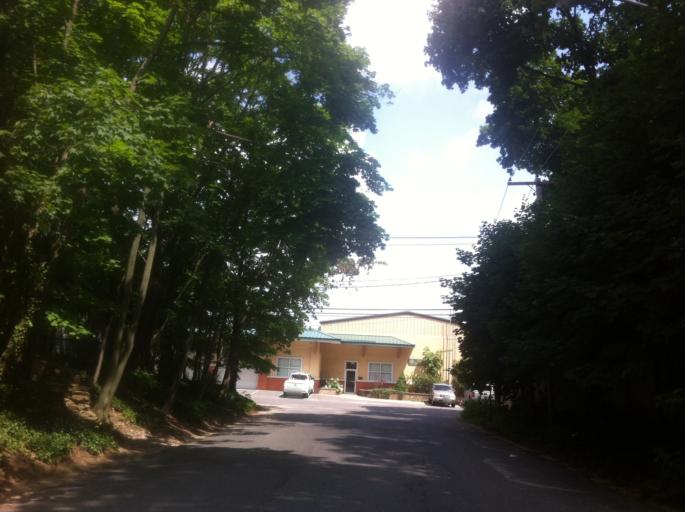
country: US
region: New York
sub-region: Nassau County
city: Sea Cliff
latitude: 40.8520
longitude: -73.6378
